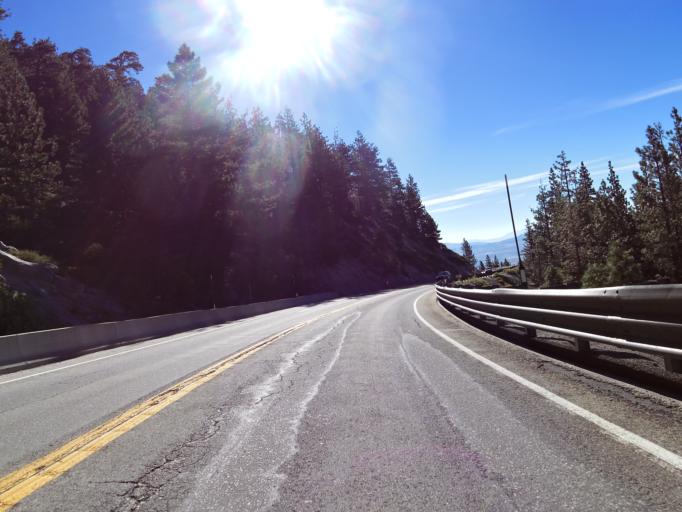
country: US
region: Nevada
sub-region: Douglas County
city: Kingsbury
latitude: 38.9758
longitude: -119.8817
